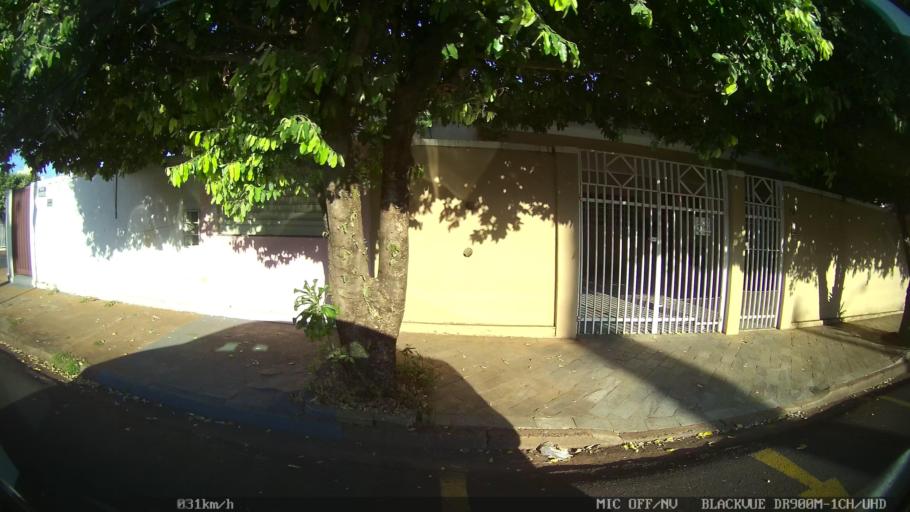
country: BR
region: Sao Paulo
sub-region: Sao Jose Do Rio Preto
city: Sao Jose do Rio Preto
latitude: -20.7990
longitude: -49.3636
